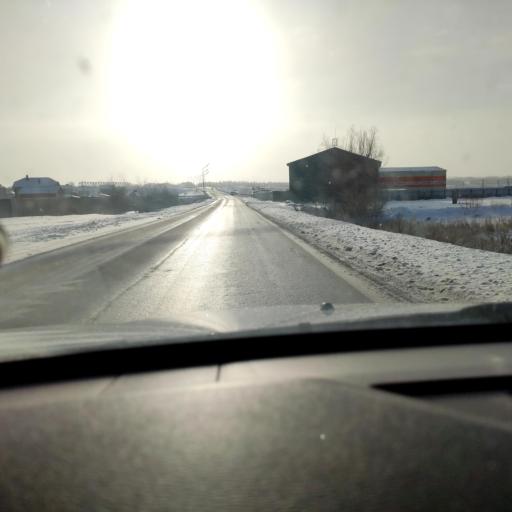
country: RU
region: Samara
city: Smyshlyayevka
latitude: 53.1571
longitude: 50.3848
